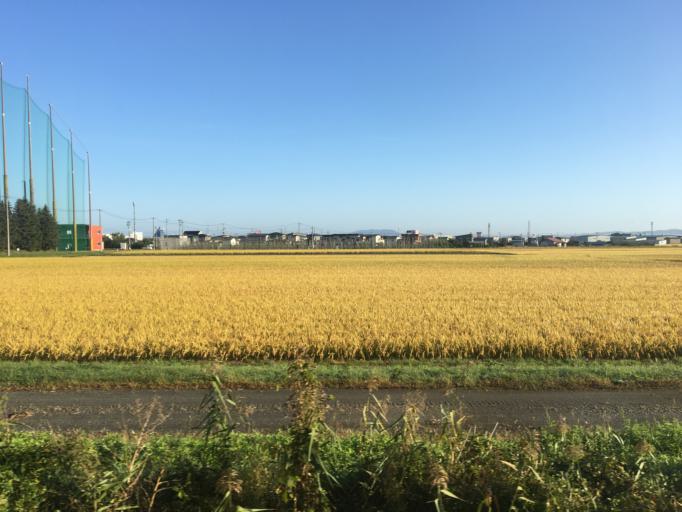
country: JP
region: Aomori
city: Hirosaki
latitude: 40.5886
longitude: 140.5096
